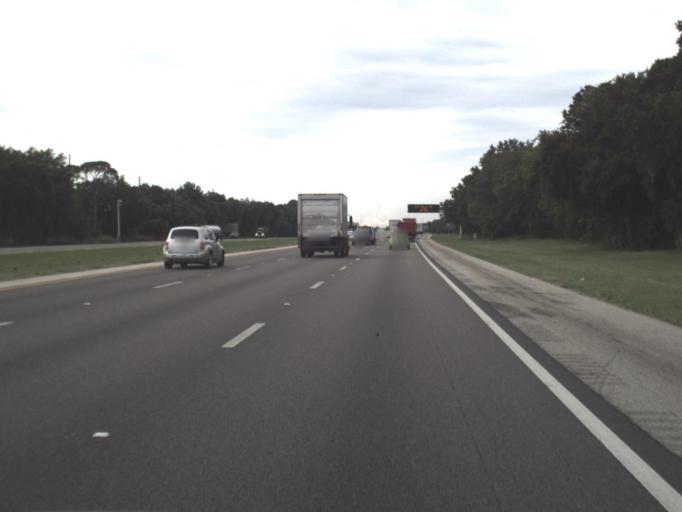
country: US
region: Florida
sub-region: Sarasota County
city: Fruitville
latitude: 27.3190
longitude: -82.4481
